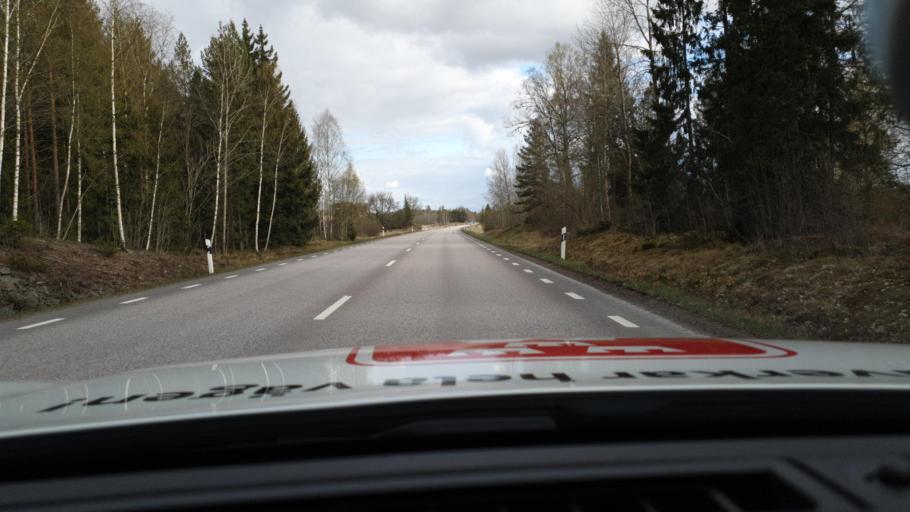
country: SE
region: Uppsala
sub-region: Osthammars Kommun
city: Bjorklinge
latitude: 59.9599
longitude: 17.3956
